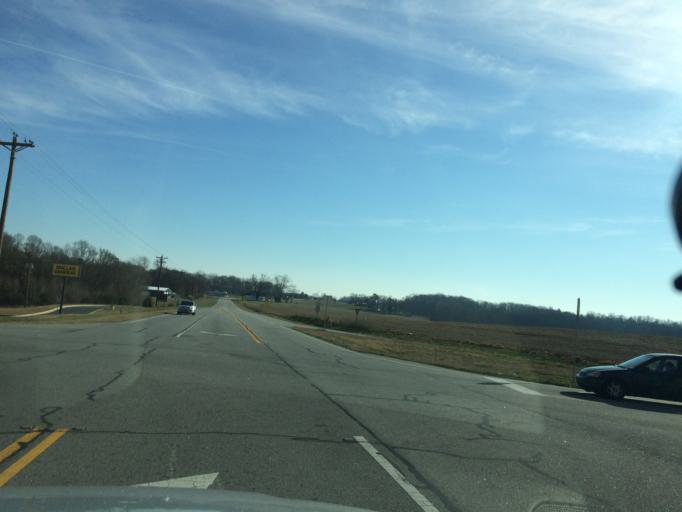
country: US
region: Georgia
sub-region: Franklin County
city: Lavonia
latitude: 34.4115
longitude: -83.0254
